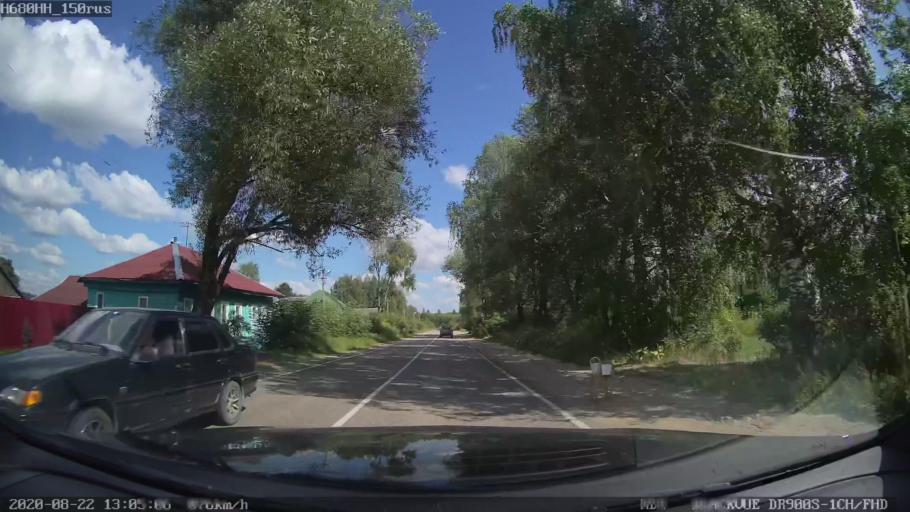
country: RU
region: Tverskaya
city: Bezhetsk
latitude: 57.6703
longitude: 36.4413
